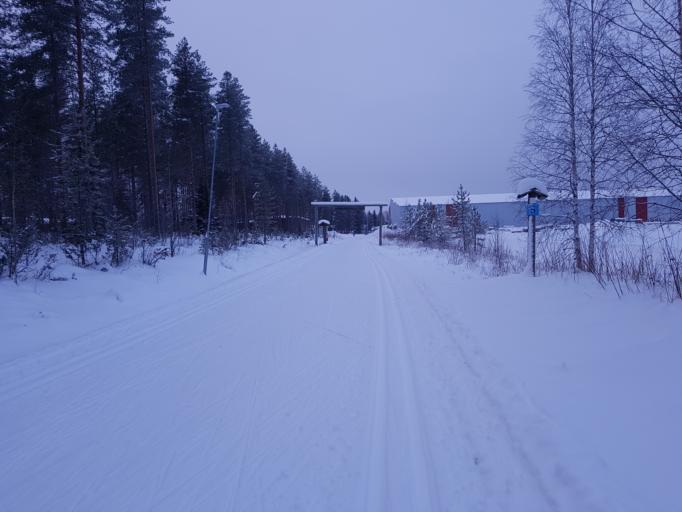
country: FI
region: Kainuu
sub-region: Kehys-Kainuu
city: Kuhmo
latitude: 64.1171
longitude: 29.5221
